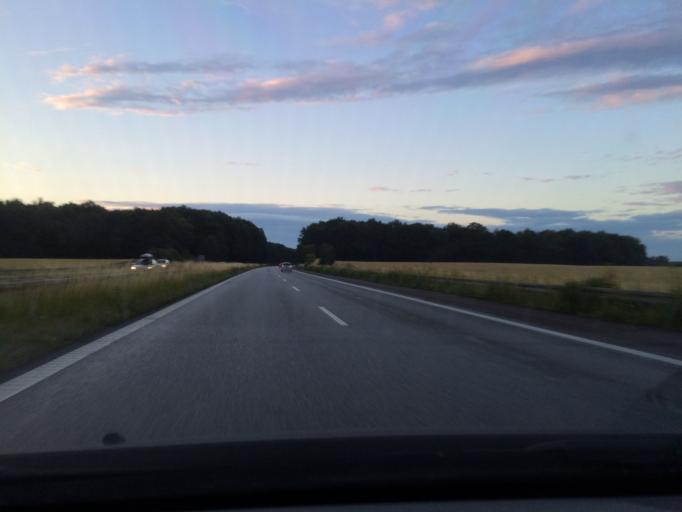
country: DK
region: Zealand
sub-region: Koge Kommune
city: Bjaeverskov
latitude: 55.3628
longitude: 12.0768
